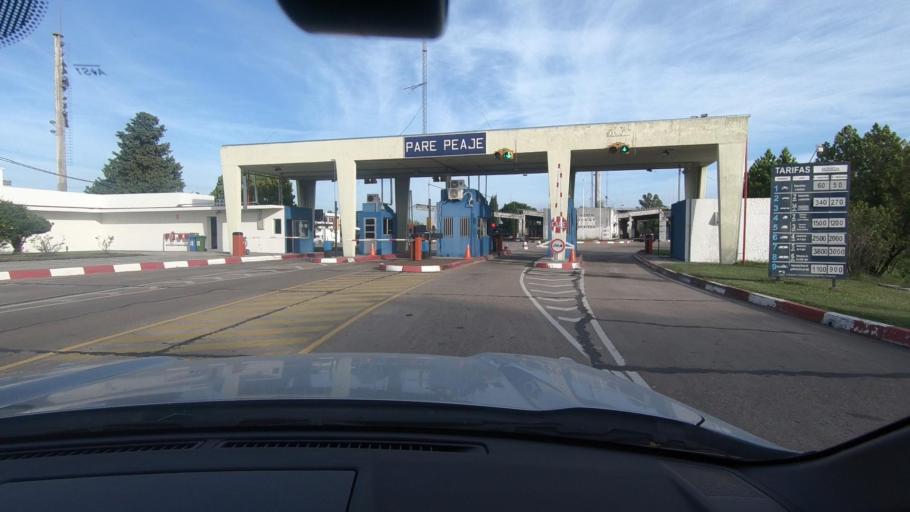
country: AR
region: Entre Rios
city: Colon
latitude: -32.2499
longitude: -58.1428
